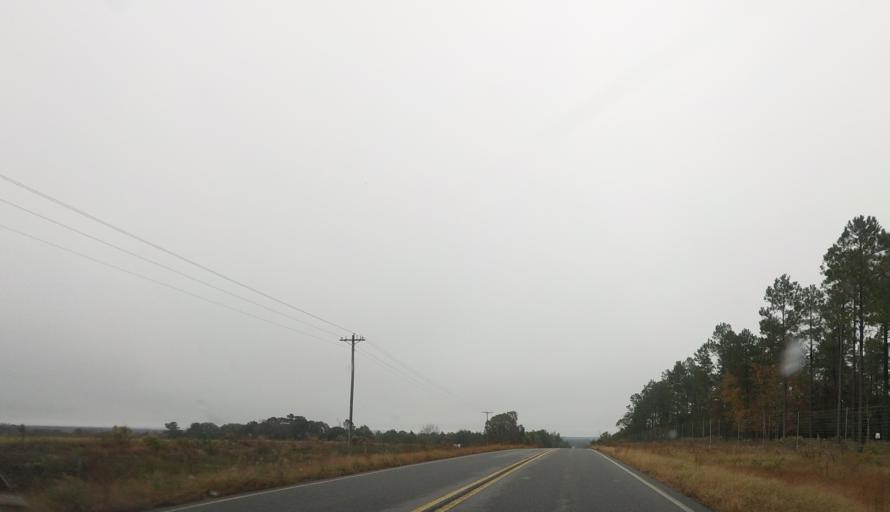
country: US
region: Georgia
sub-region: Marion County
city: Buena Vista
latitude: 32.4104
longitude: -84.4032
